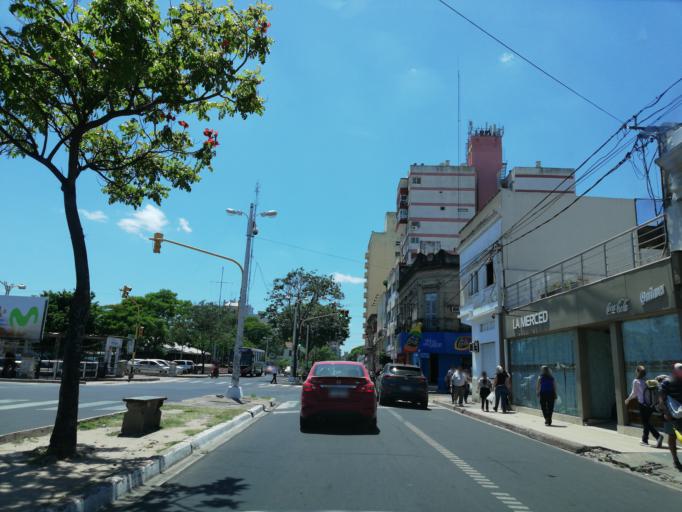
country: AR
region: Corrientes
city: Corrientes
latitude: -27.4618
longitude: -58.8379
